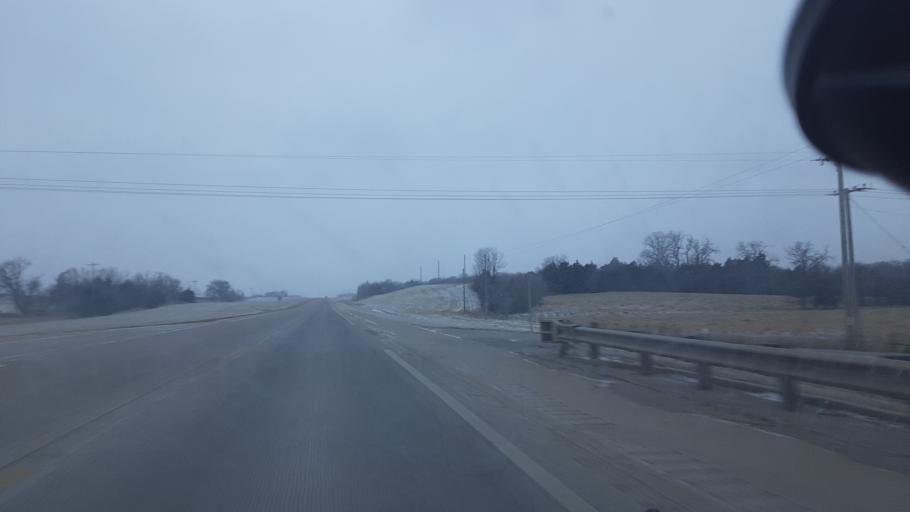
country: US
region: Oklahoma
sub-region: Payne County
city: Perkins
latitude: 35.9860
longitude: -97.1226
